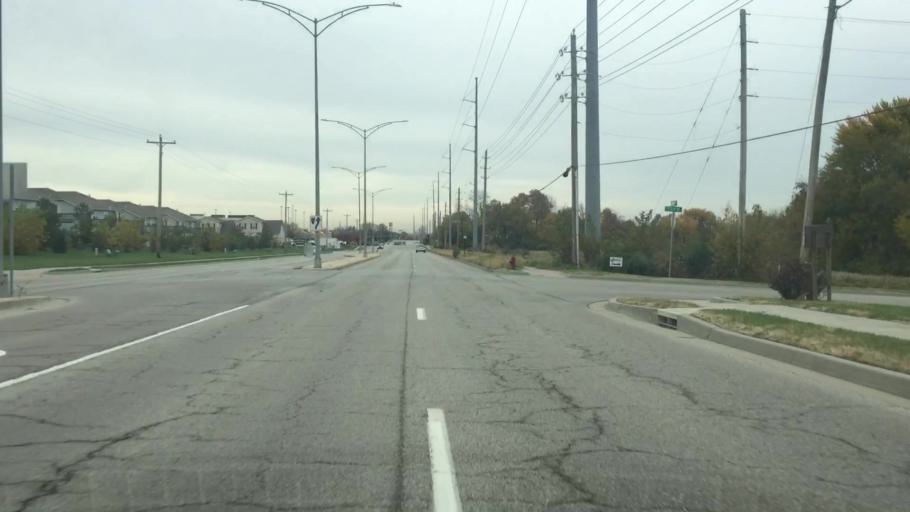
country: US
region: Missouri
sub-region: Cass County
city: Belton
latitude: 38.8091
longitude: -94.5125
